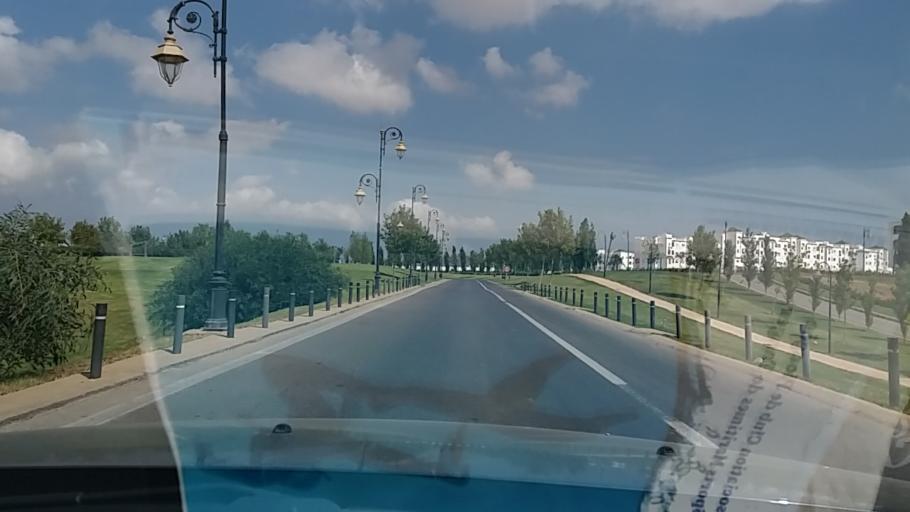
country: MA
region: Tanger-Tetouan
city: Tetouan
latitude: 35.5982
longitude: -5.3368
